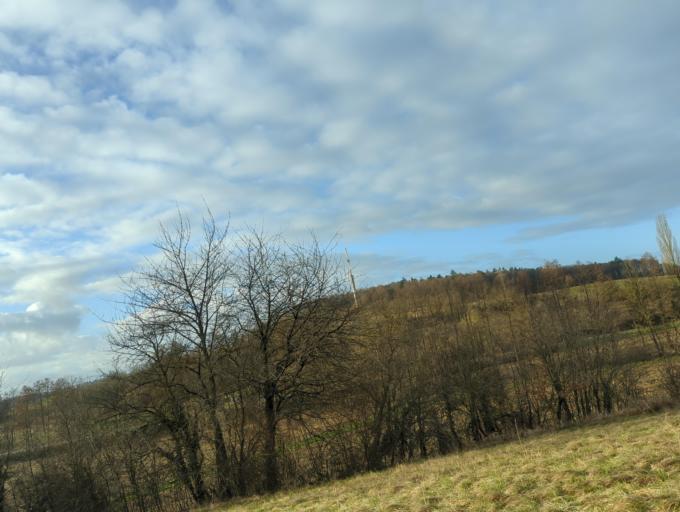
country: DE
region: Baden-Wuerttemberg
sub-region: Karlsruhe Region
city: Joehlingen
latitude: 49.0240
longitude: 8.5896
